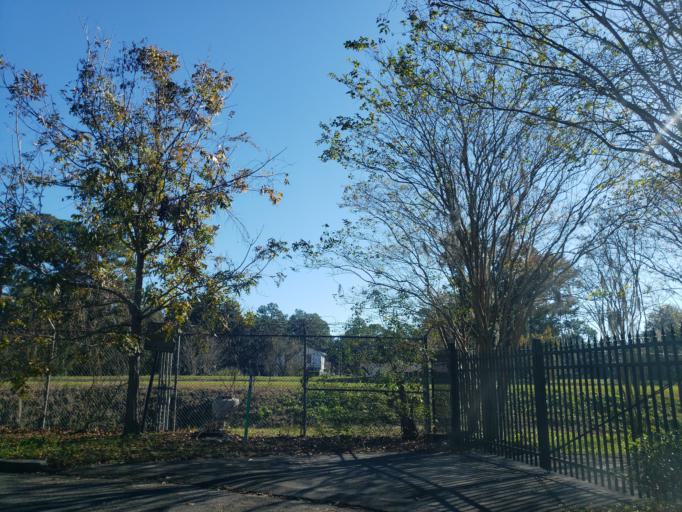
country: US
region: Georgia
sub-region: Chatham County
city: Isle of Hope
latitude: 31.9942
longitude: -81.1015
